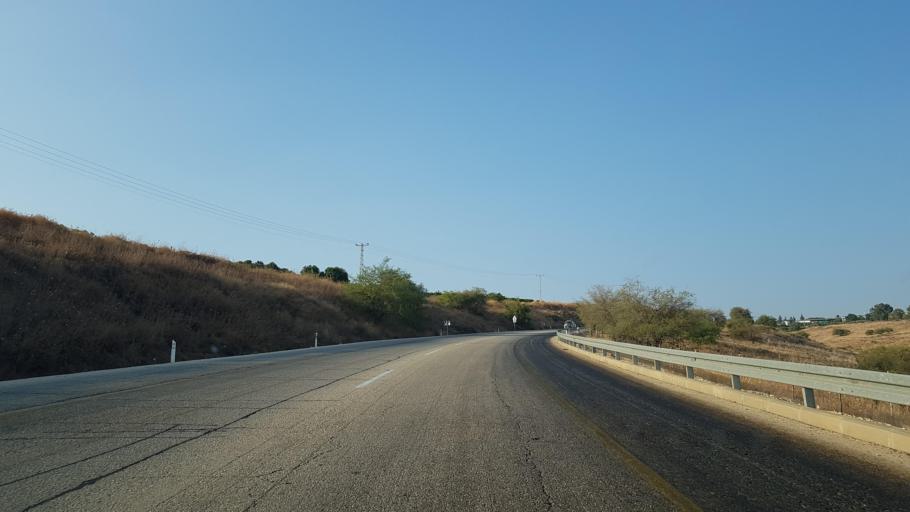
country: SY
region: Quneitra
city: Al Butayhah
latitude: 32.8984
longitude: 35.5967
